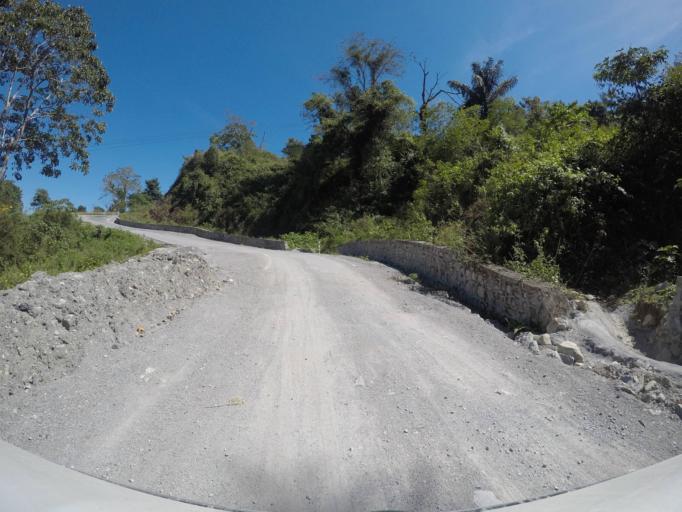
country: TL
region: Manufahi
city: Same
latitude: -8.9061
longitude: 125.9765
